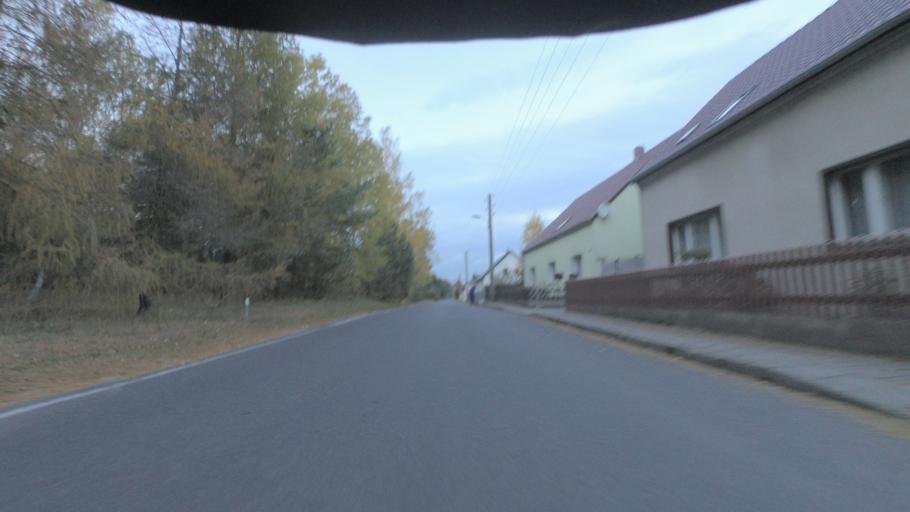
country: DE
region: Brandenburg
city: Sonnewalde
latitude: 51.7694
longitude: 13.6183
